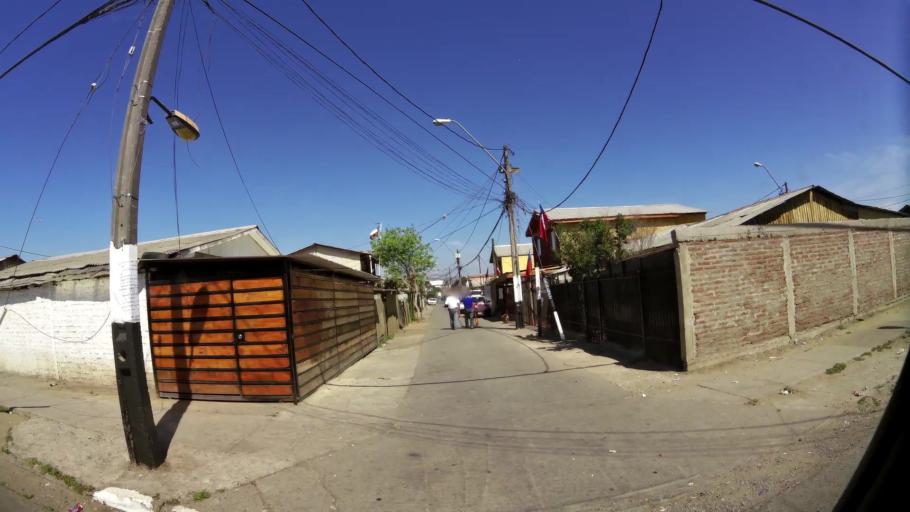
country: CL
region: Santiago Metropolitan
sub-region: Provincia de Santiago
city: Lo Prado
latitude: -33.5134
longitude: -70.7442
